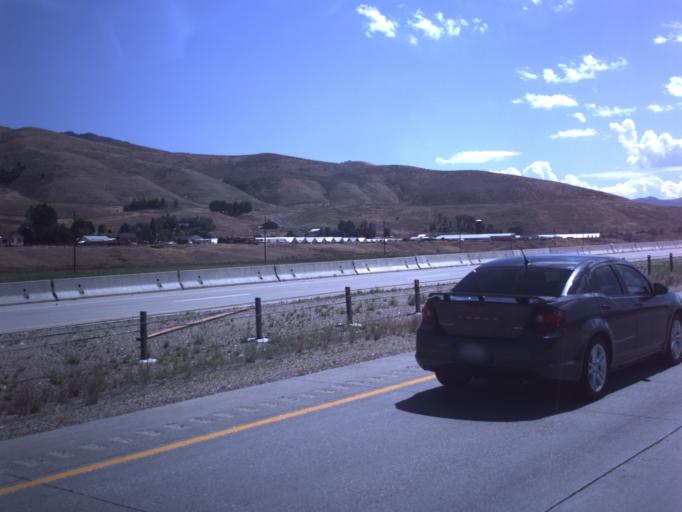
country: US
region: Utah
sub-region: Morgan County
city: Mountain Green
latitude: 41.1006
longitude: -111.7436
